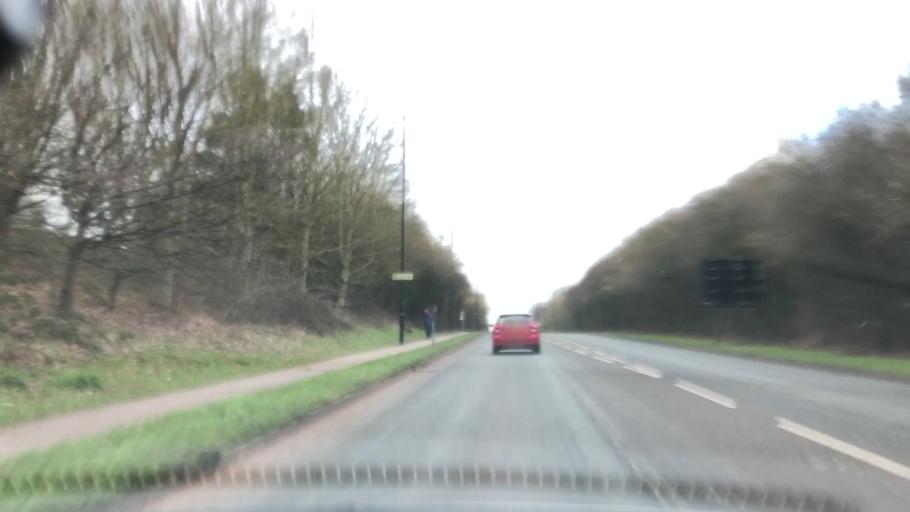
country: GB
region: England
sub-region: Coventry
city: Keresley
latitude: 52.4355
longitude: -1.5519
